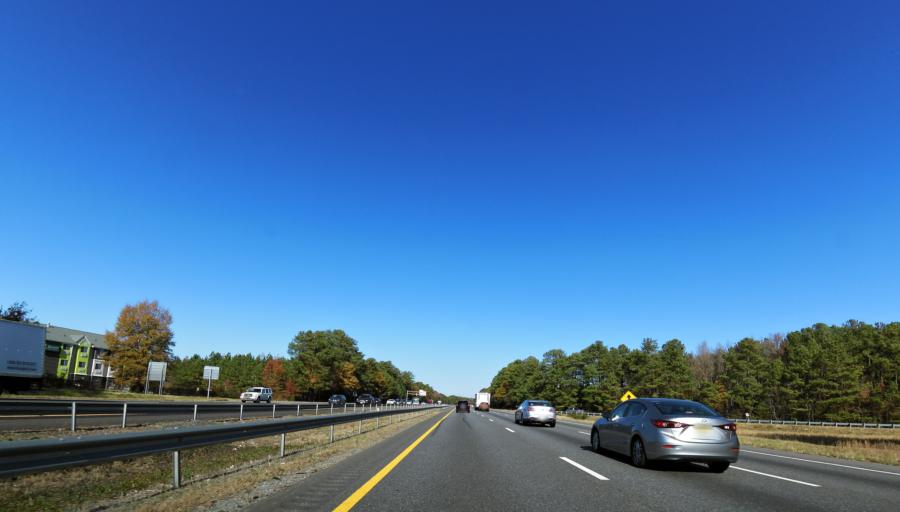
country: US
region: Virginia
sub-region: Hanover County
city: Ashland
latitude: 37.7613
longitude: -77.4596
